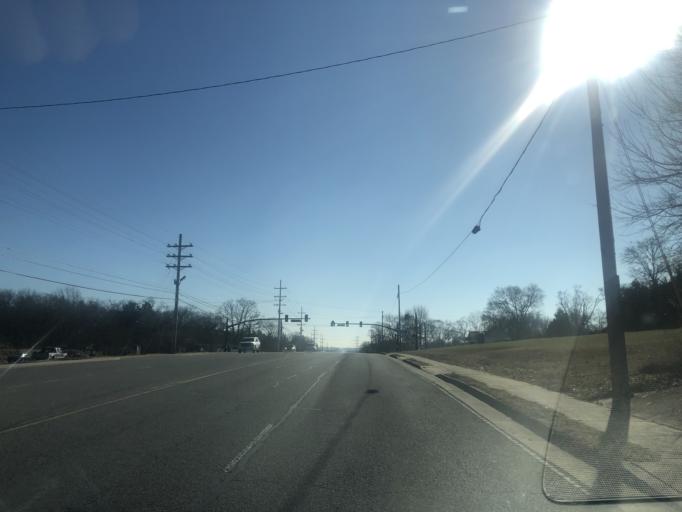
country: US
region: Tennessee
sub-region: Rutherford County
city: Smyrna
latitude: 35.9730
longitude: -86.5349
